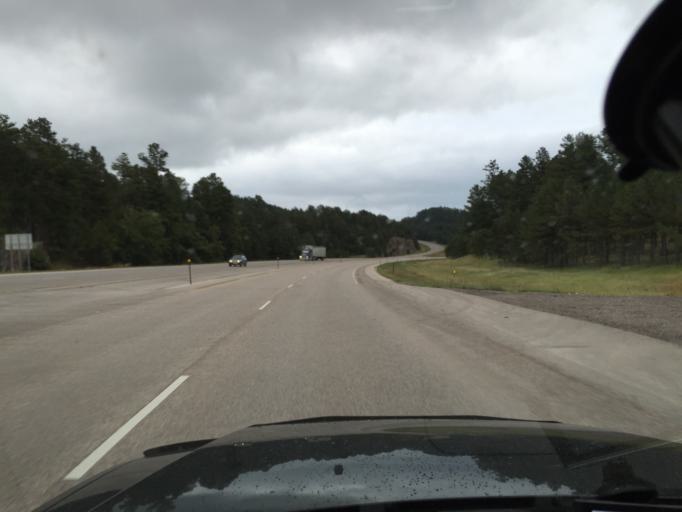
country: US
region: South Dakota
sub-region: Pennington County
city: Colonial Pine Hills
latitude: 43.9434
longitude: -103.3935
